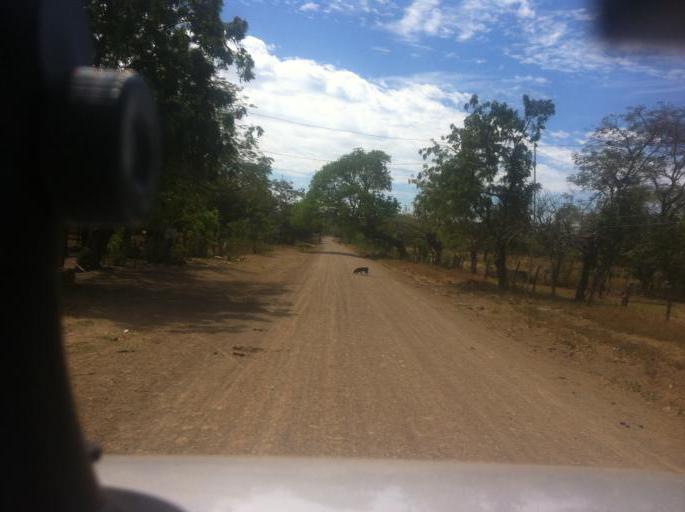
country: NI
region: Granada
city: Nandaime
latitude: 11.6222
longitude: -86.0252
